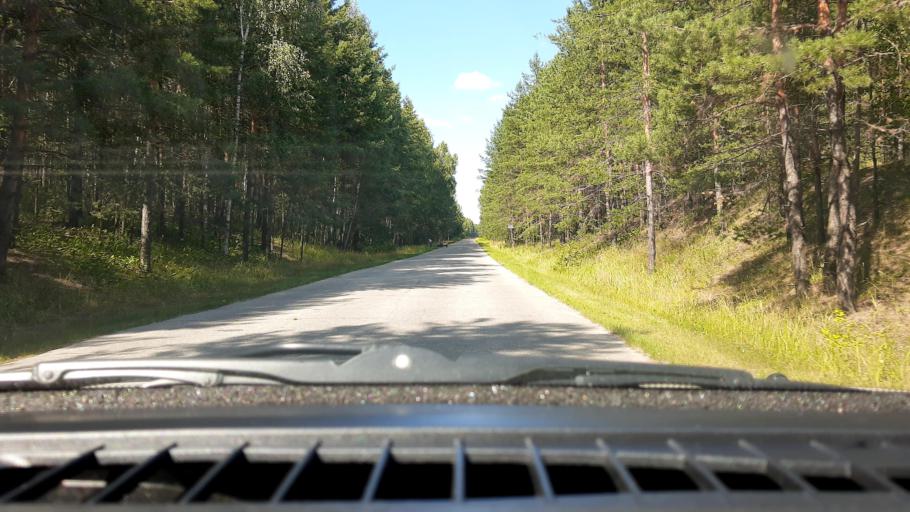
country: RU
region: Nizjnij Novgorod
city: Babino
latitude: 56.3258
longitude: 43.6343
